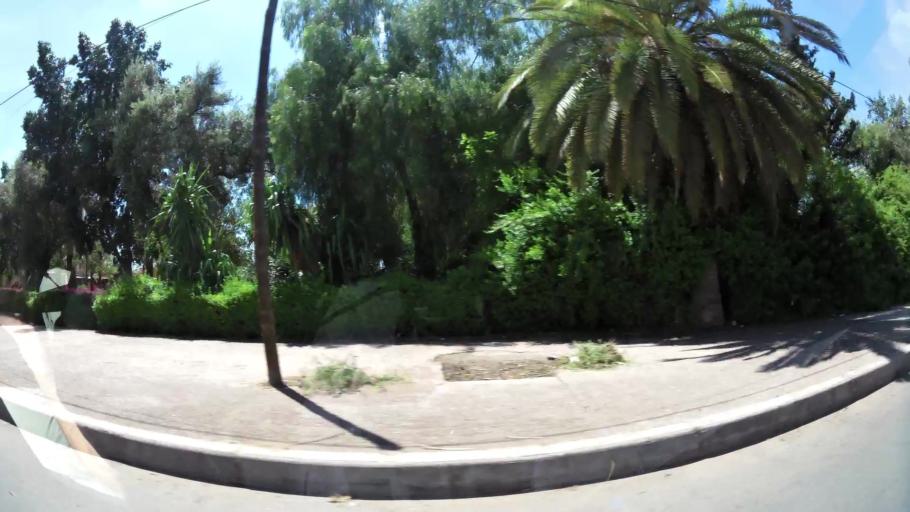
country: MA
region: Marrakech-Tensift-Al Haouz
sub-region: Marrakech
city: Marrakesh
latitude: 31.6325
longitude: -8.0420
